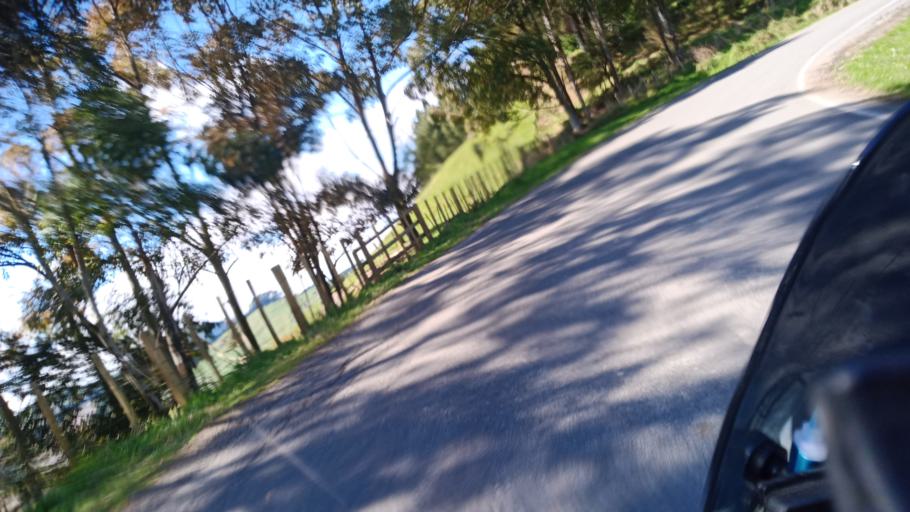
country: NZ
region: Gisborne
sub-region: Gisborne District
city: Gisborne
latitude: -38.7880
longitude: 177.7827
